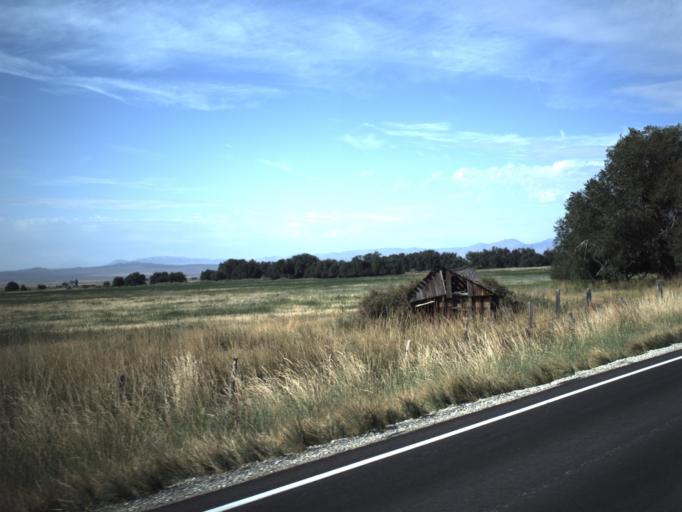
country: US
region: Idaho
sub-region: Cassia County
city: Burley
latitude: 41.8171
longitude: -113.3118
